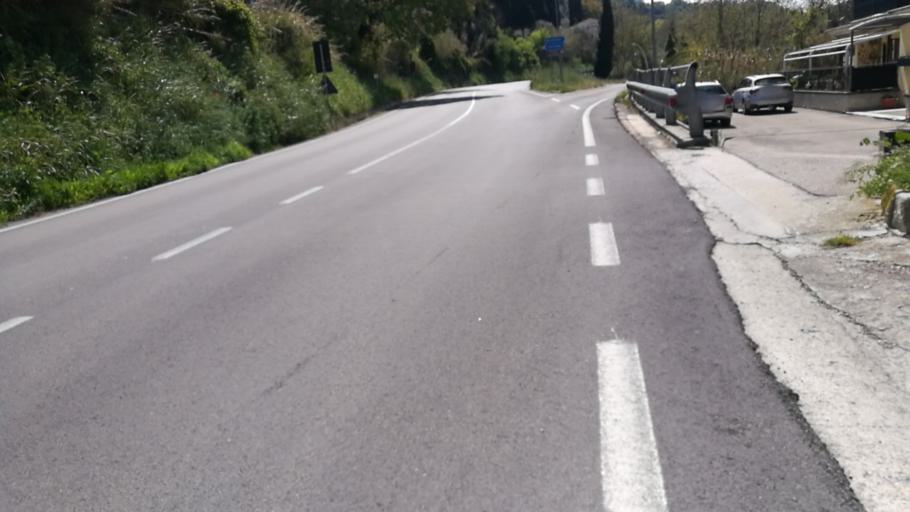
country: IT
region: Abruzzo
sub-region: Provincia di Chieti
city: Marina di San Vito
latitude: 42.3034
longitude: 14.4423
